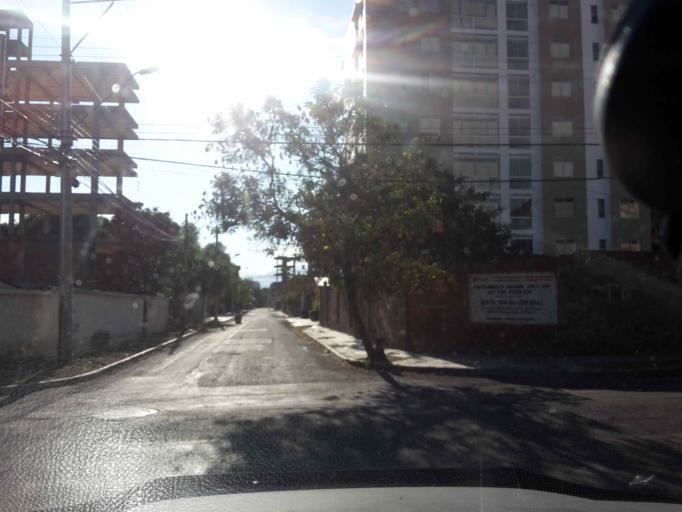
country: BO
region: Cochabamba
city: Cochabamba
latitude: -17.3734
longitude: -66.1768
